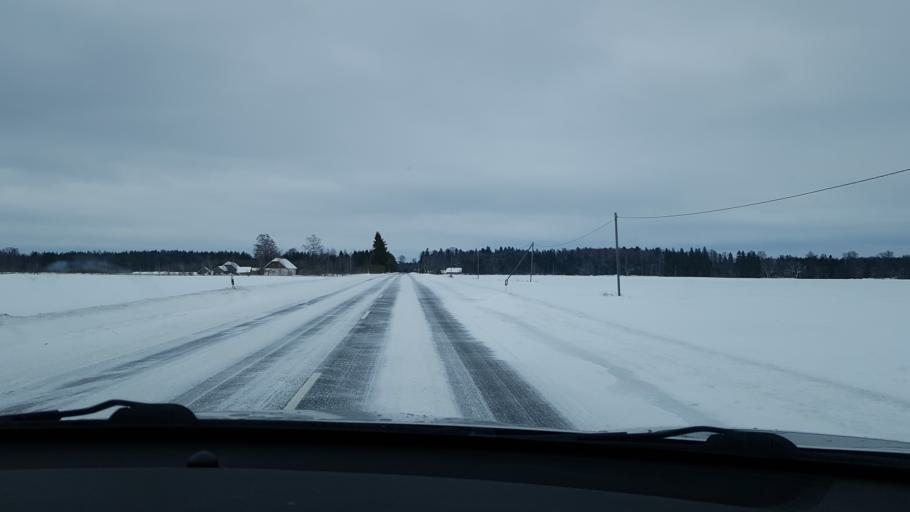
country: EE
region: Jaervamaa
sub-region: Jaerva-Jaani vald
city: Jarva-Jaani
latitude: 59.1090
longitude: 25.8010
